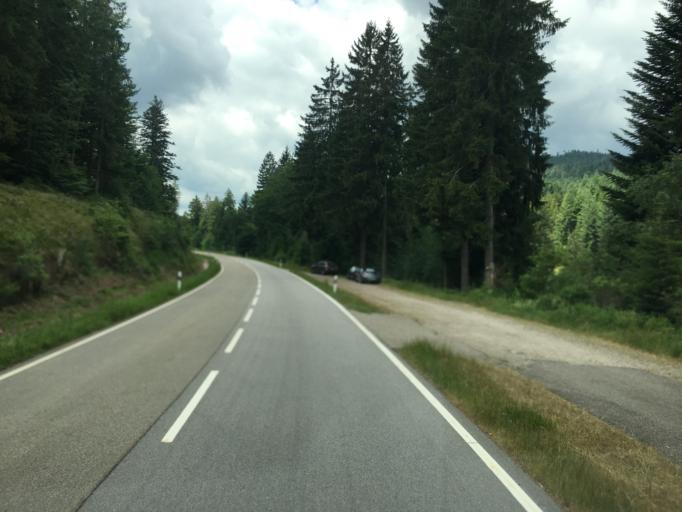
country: DE
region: Baden-Wuerttemberg
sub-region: Karlsruhe Region
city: Forbach
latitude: 48.6615
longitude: 8.3131
